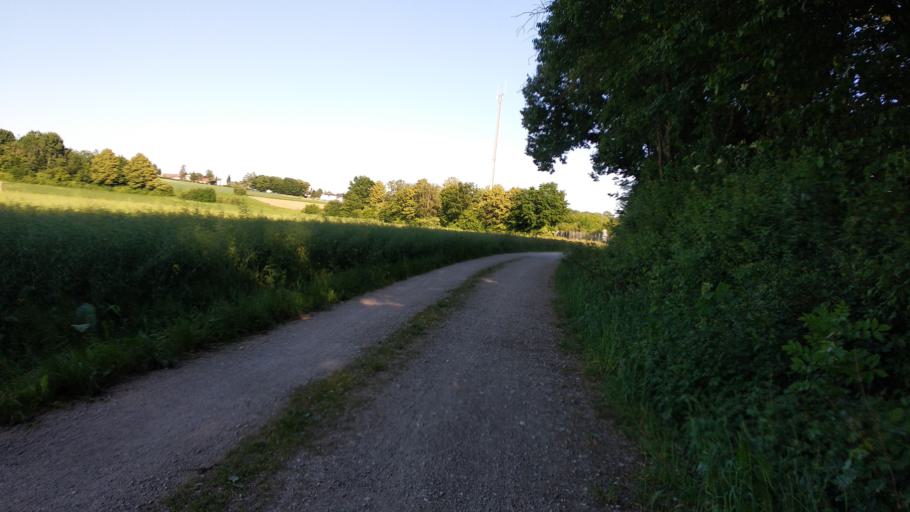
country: DE
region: Bavaria
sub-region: Upper Bavaria
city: Zorneding
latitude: 48.0958
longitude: 11.8190
